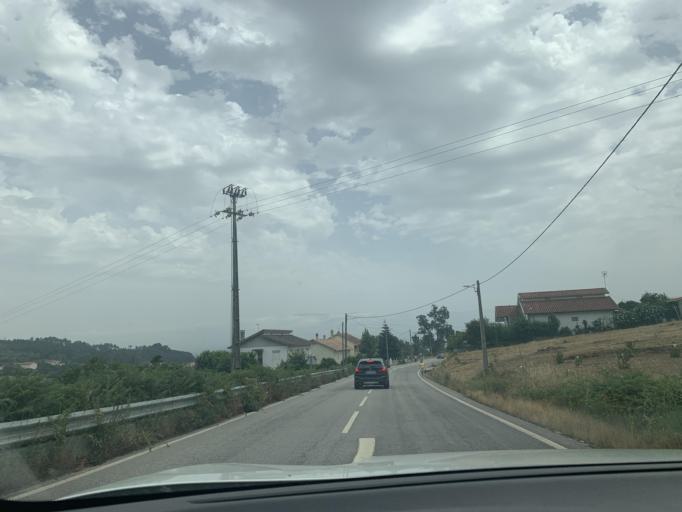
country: PT
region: Viseu
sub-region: Mangualde
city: Mangualde
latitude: 40.5705
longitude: -7.7247
